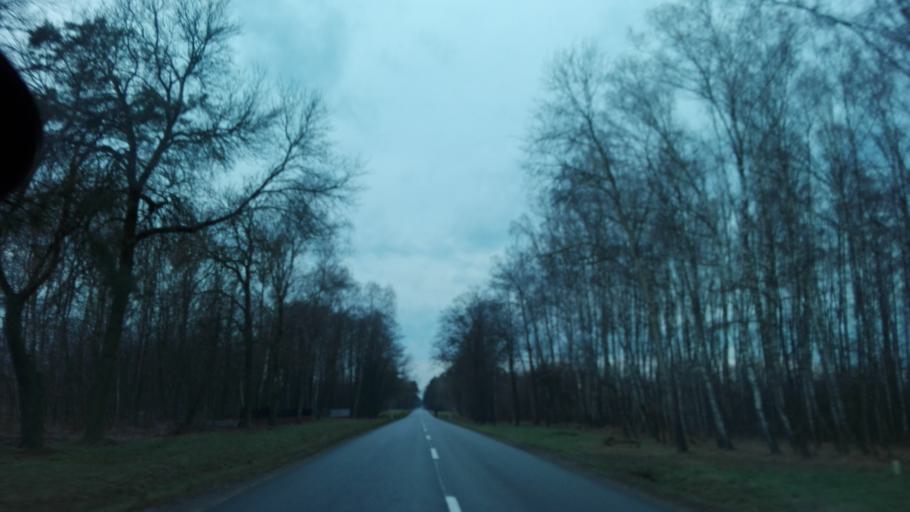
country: PL
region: Lublin Voivodeship
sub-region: Powiat radzynski
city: Wohyn
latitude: 51.7804
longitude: 22.7100
